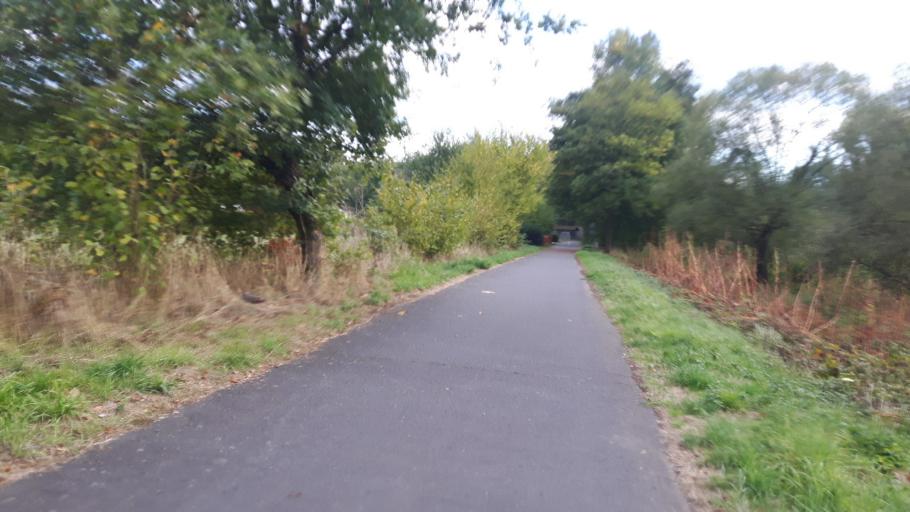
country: DE
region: Rheinland-Pfalz
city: Werkhausen
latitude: 50.7635
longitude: 7.5043
